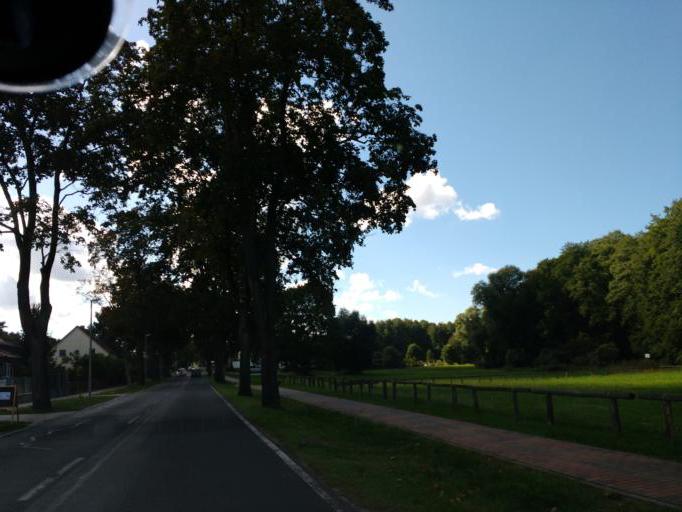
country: DE
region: Brandenburg
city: Mittenwalde
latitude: 52.2111
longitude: 13.5850
